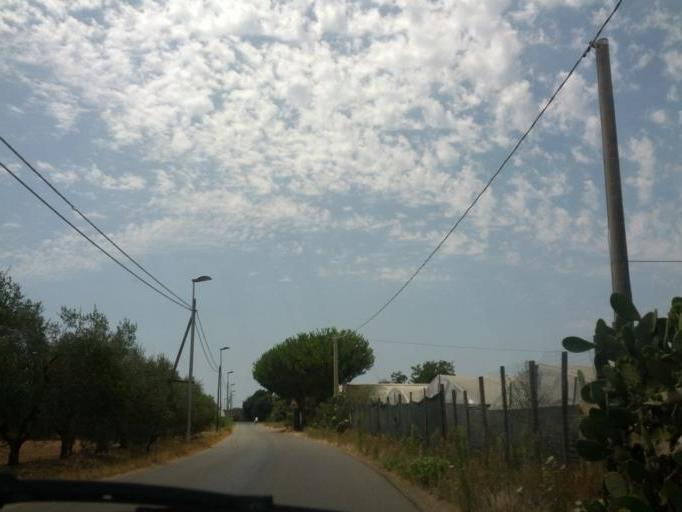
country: IT
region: Latium
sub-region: Provincia di Latina
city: Sperlonga
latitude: 41.2911
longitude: 13.3930
